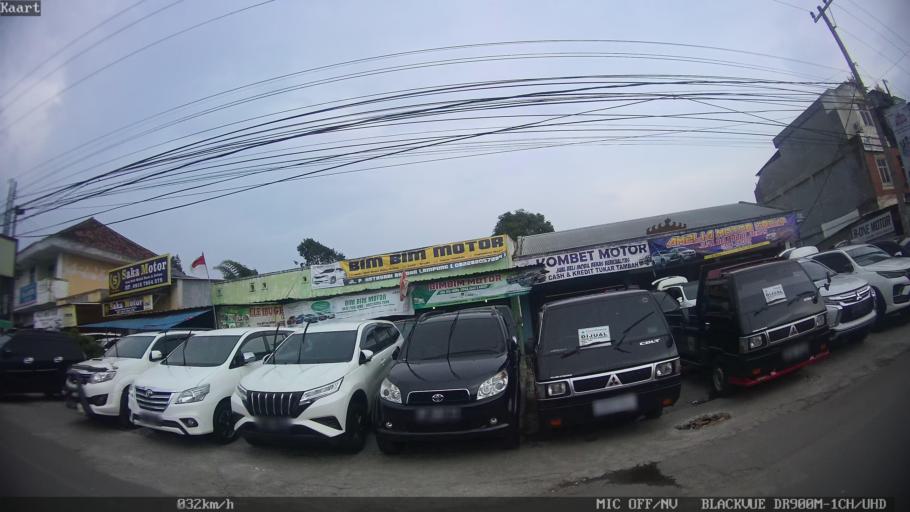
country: ID
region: Lampung
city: Kedaton
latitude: -5.4011
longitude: 105.2860
